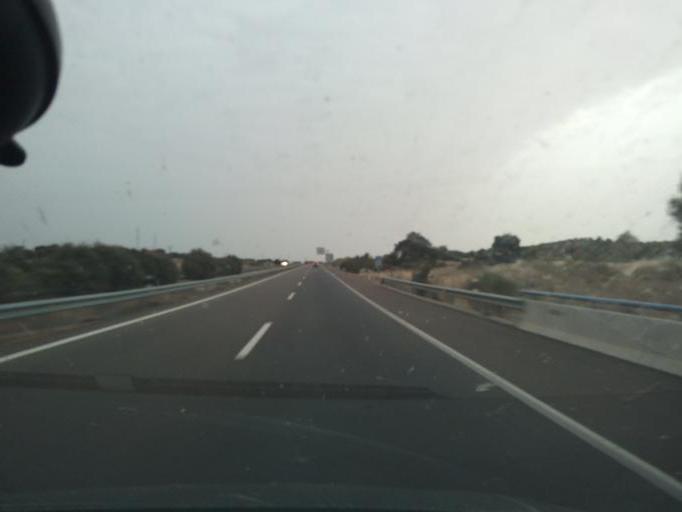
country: ES
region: Extremadura
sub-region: Provincia de Badajoz
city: San Pedro de Merida
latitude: 38.9496
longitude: -6.1708
